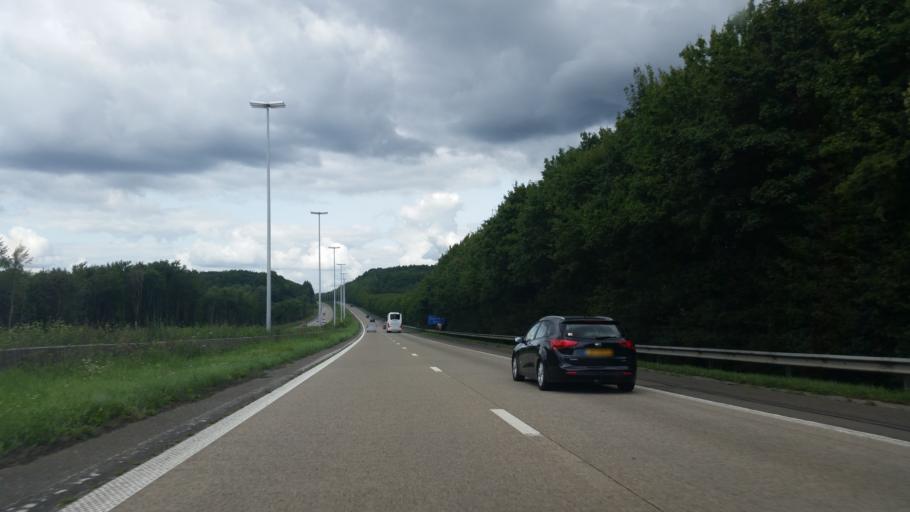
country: BE
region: Wallonia
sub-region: Province de Namur
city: Assesse
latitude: 50.3630
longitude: 5.0025
